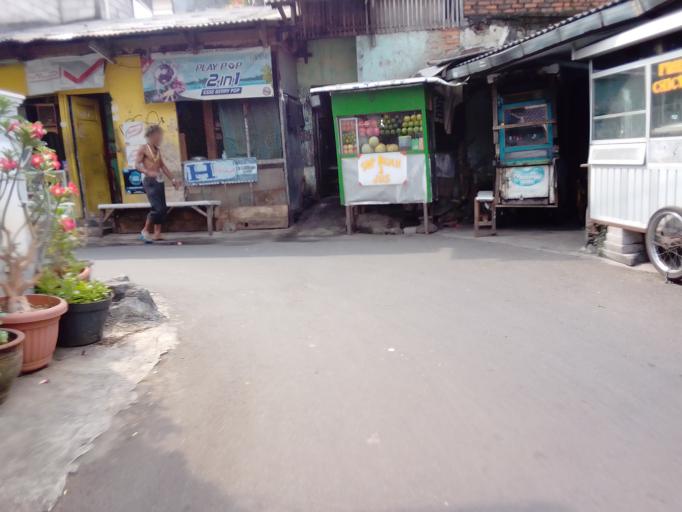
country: ID
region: Jakarta Raya
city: Jakarta
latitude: -6.1974
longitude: 106.8057
